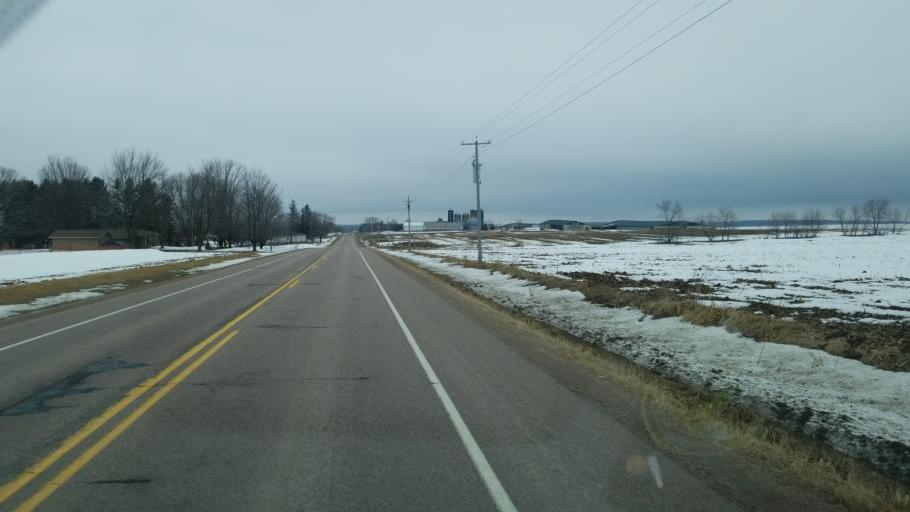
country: US
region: Wisconsin
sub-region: Wood County
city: Marshfield
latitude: 44.6361
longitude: -90.2183
